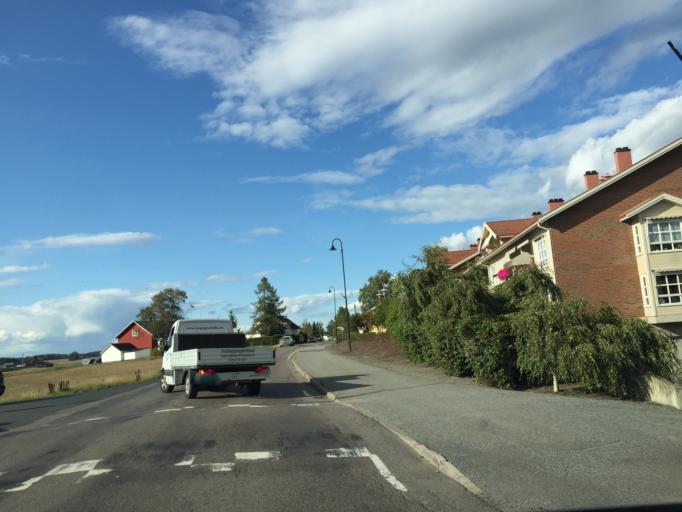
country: NO
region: Ostfold
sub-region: Trogstad
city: Skjonhaug
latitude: 59.6421
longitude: 11.3157
